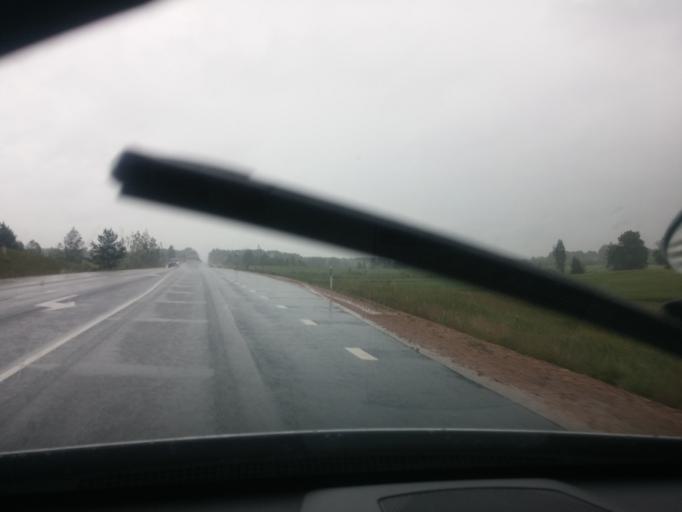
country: LV
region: Ikskile
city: Ikskile
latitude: 56.8853
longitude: 24.4959
